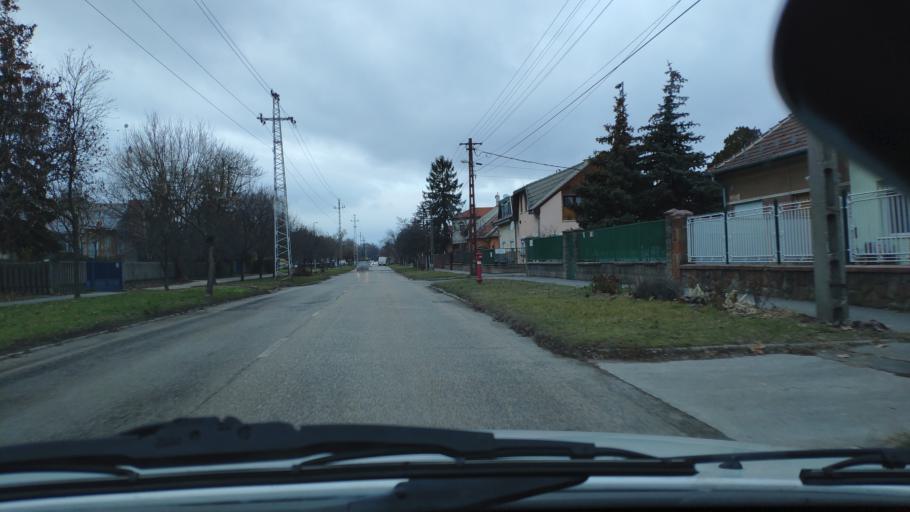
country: HU
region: Budapest
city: Budapest XXI. keruelet
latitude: 47.4077
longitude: 19.0756
